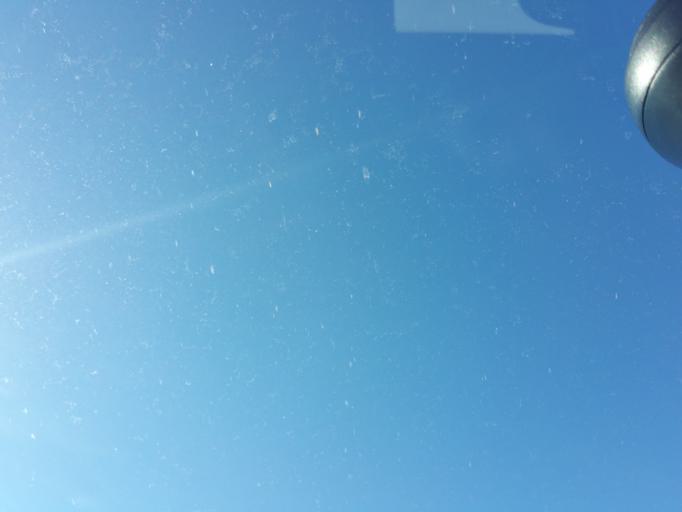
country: US
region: Iowa
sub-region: Decatur County
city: Lamoni
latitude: 40.6444
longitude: -93.8683
